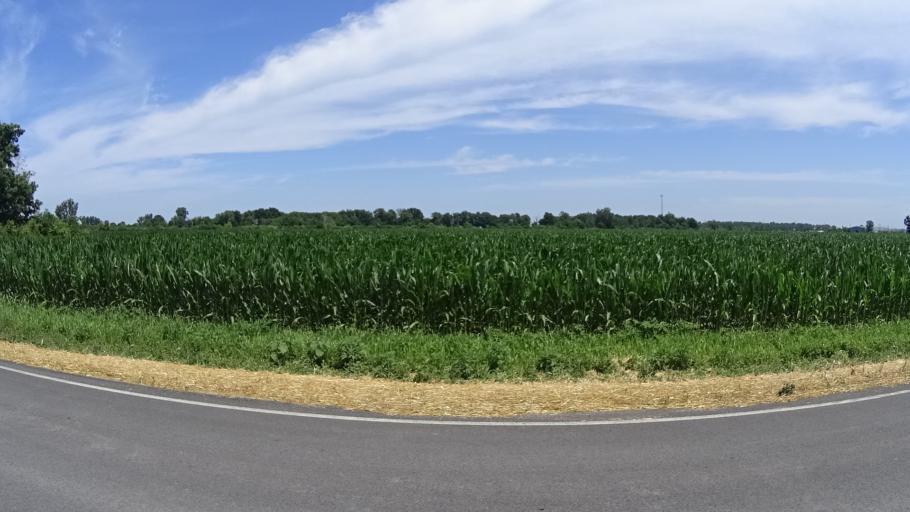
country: US
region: Ohio
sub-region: Erie County
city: Sandusky
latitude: 41.4240
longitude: -82.7721
